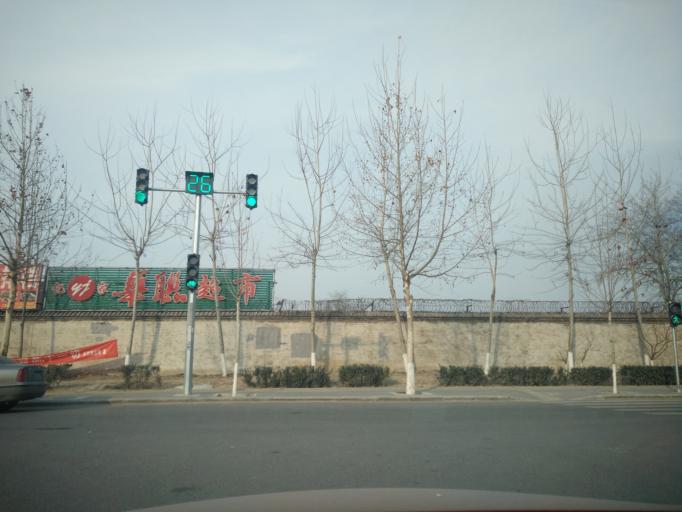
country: CN
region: Beijing
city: Yinghai
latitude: 39.7171
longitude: 116.3960
